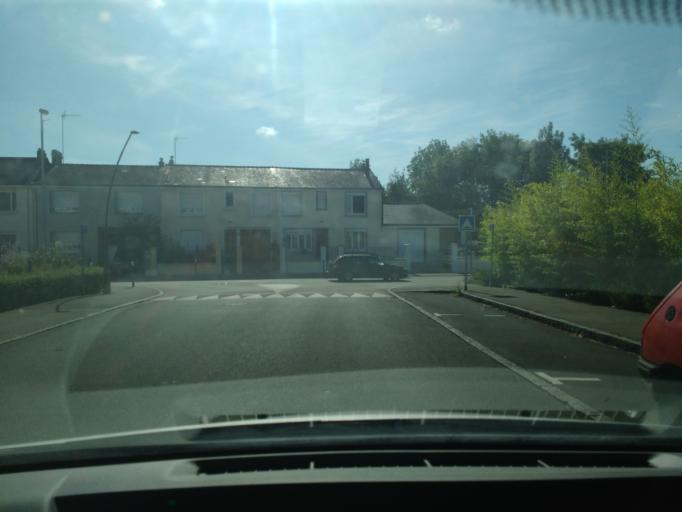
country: FR
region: Pays de la Loire
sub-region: Departement de Maine-et-Loire
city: Angers
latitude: 47.4661
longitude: -0.5098
